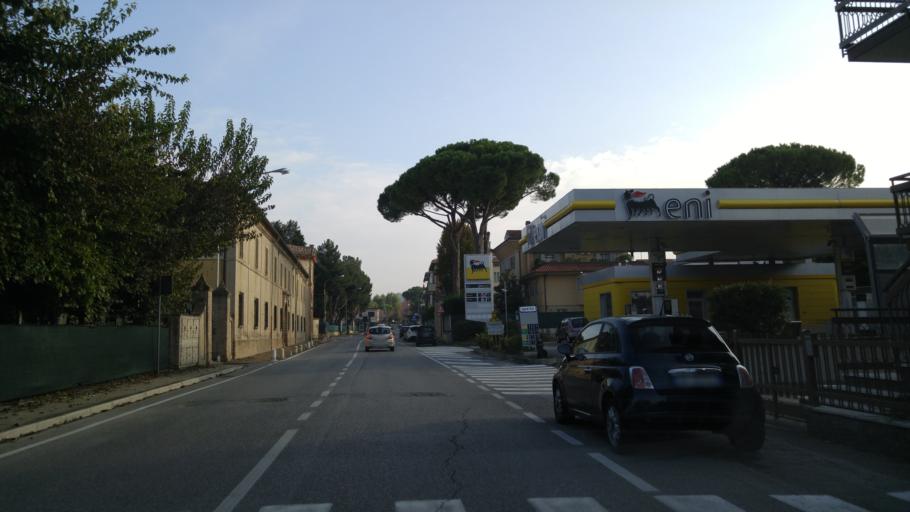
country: IT
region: The Marches
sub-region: Provincia di Pesaro e Urbino
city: Pesaro
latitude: 43.8933
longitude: 12.9231
